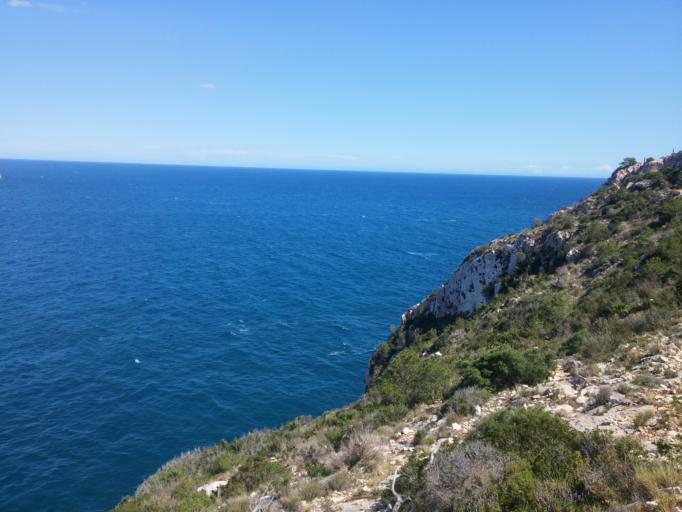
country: ES
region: Valencia
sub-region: Provincia de Alicante
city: Benitachell
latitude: 38.7266
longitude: 0.1978
